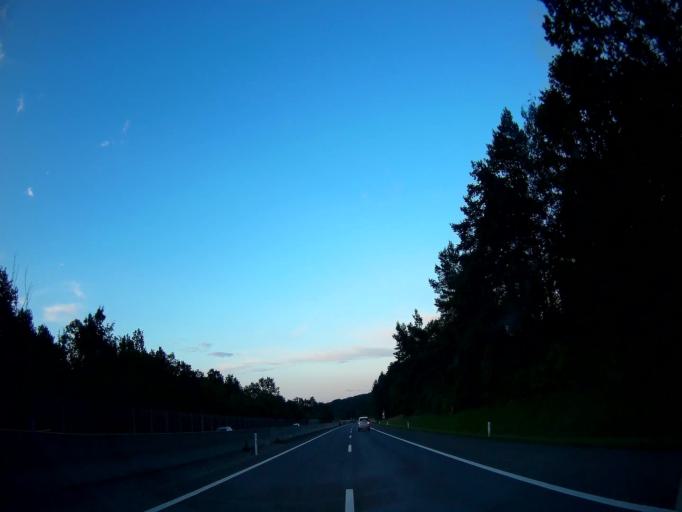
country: AT
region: Lower Austria
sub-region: Politischer Bezirk Modling
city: Laab im Walde
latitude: 48.1786
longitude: 16.1655
